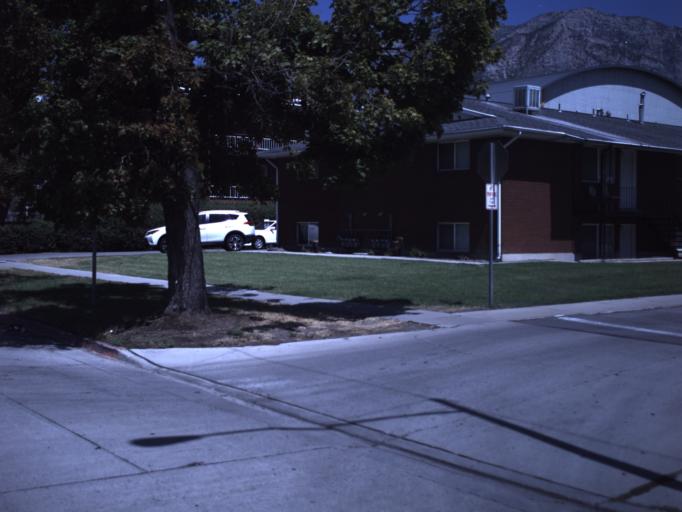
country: US
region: Utah
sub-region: Utah County
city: Provo
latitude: 40.2457
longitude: -111.6586
